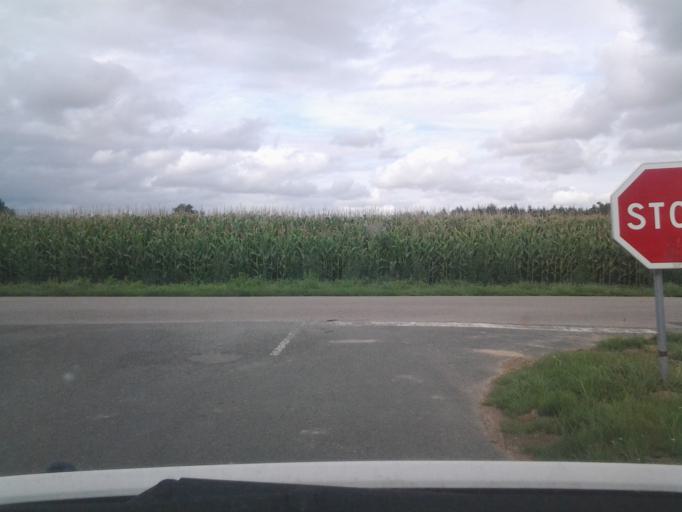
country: FR
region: Pays de la Loire
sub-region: Departement de la Vendee
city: Dompierre-sur-Yon
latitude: 46.7051
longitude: -1.3758
